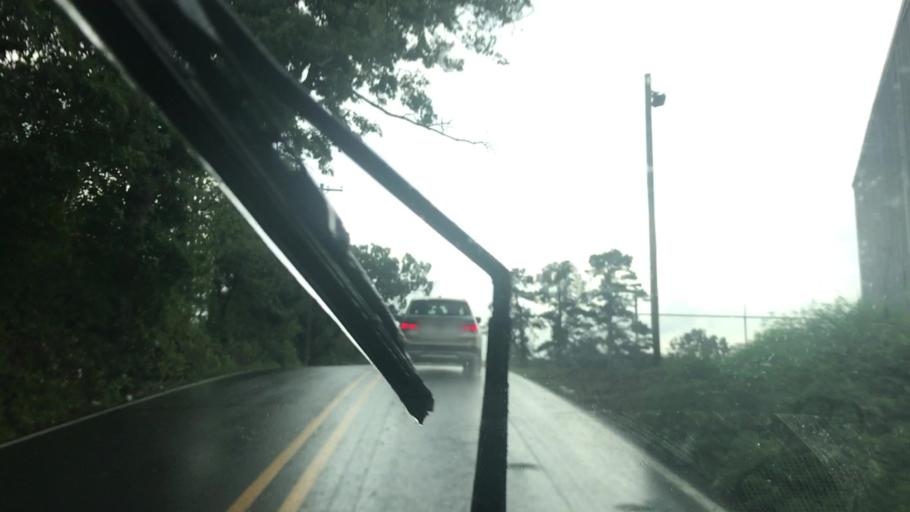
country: US
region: Arkansas
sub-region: Garland County
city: Rockwell
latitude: 34.4620
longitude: -93.1399
